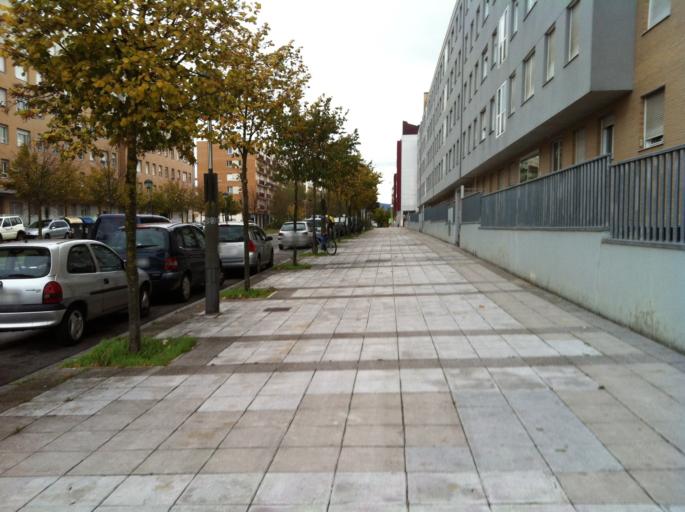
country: ES
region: Basque Country
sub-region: Provincia de Alava
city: Gasteiz / Vitoria
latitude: 42.8692
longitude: -2.6938
